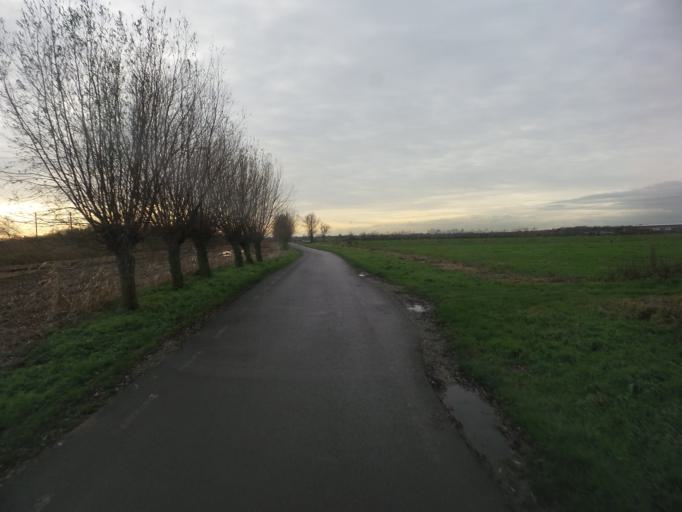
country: NL
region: South Holland
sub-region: Gemeente Vlist
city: Haastrecht
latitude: 52.0214
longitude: 4.7944
